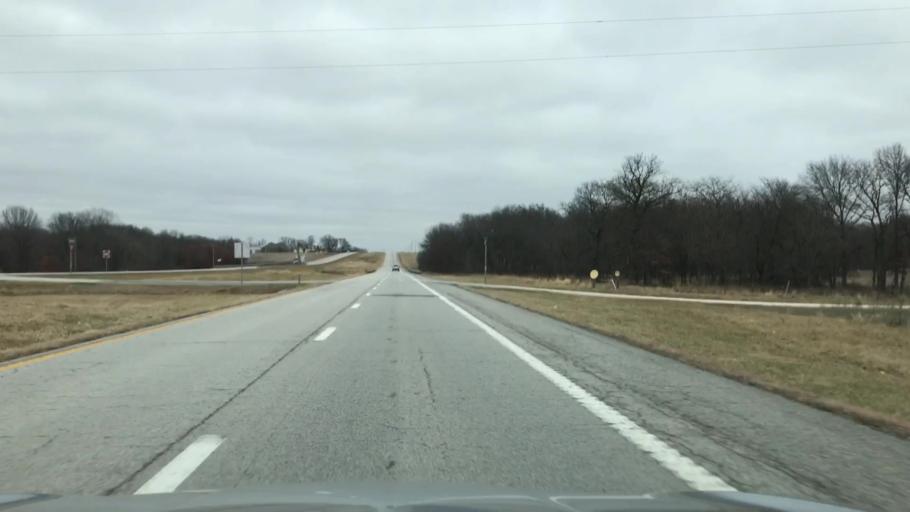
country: US
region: Missouri
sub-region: Linn County
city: Linneus
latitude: 39.7776
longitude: -93.2696
